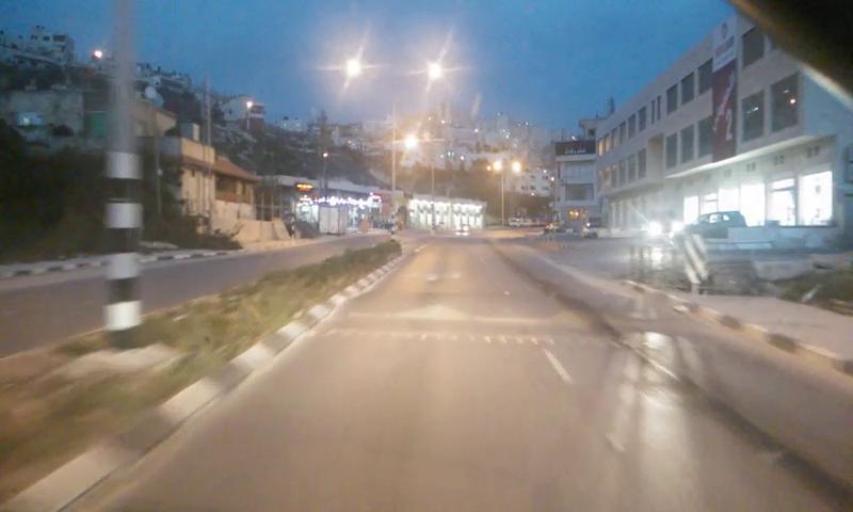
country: PS
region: West Bank
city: Zawata
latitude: 32.2412
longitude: 35.2267
